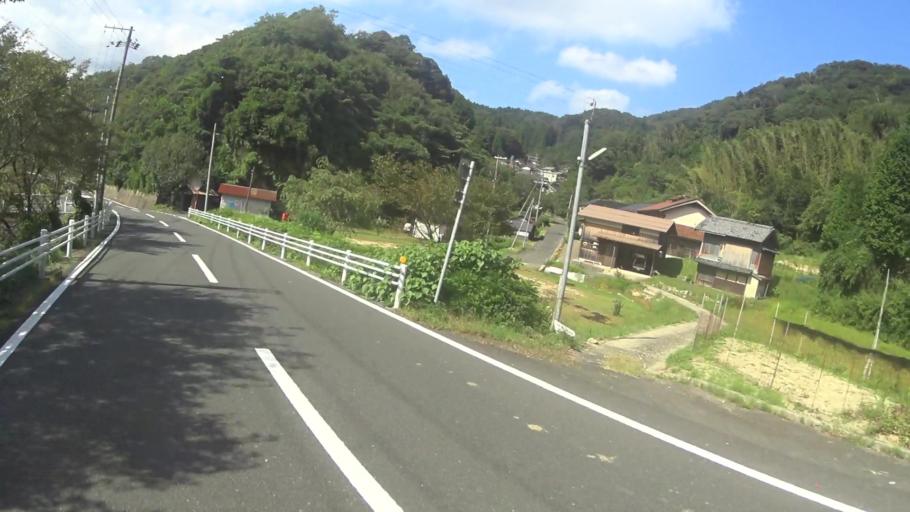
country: JP
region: Kyoto
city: Miyazu
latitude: 35.7079
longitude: 135.2726
